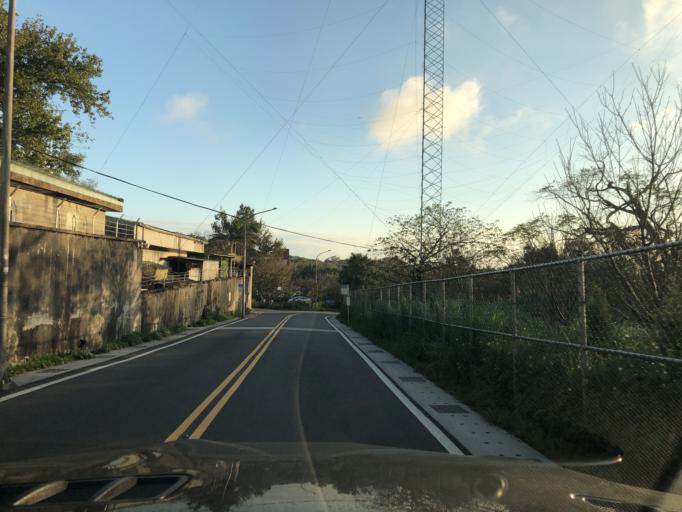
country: TW
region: Taipei
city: Taipei
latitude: 25.1445
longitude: 121.5575
